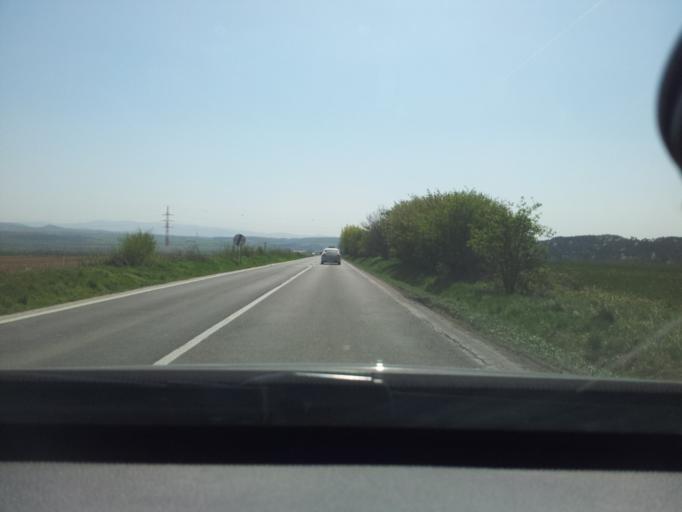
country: SK
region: Nitriansky
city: Banovce nad Bebravou
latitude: 48.7542
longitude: 18.2067
